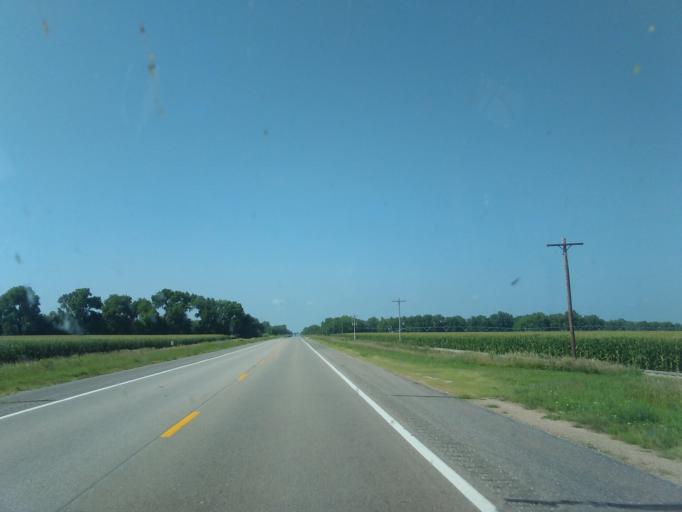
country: US
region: Nebraska
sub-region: Buffalo County
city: Kearney
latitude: 40.6456
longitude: -98.9515
